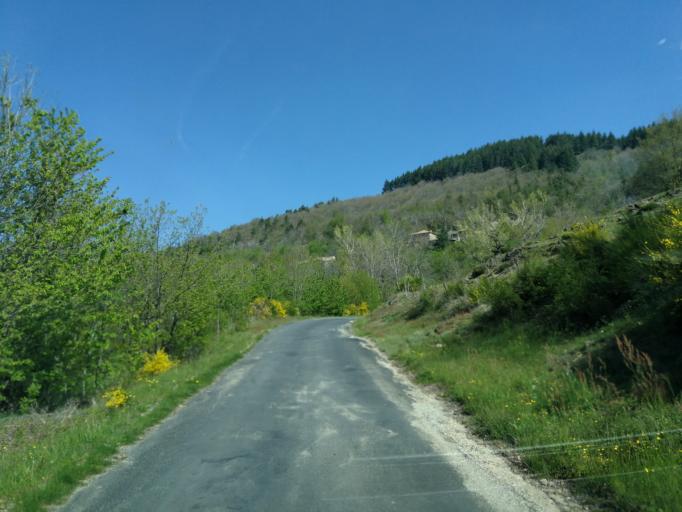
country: FR
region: Rhone-Alpes
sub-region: Departement de l'Ardeche
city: Le Cheylard
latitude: 44.9201
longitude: 4.4227
